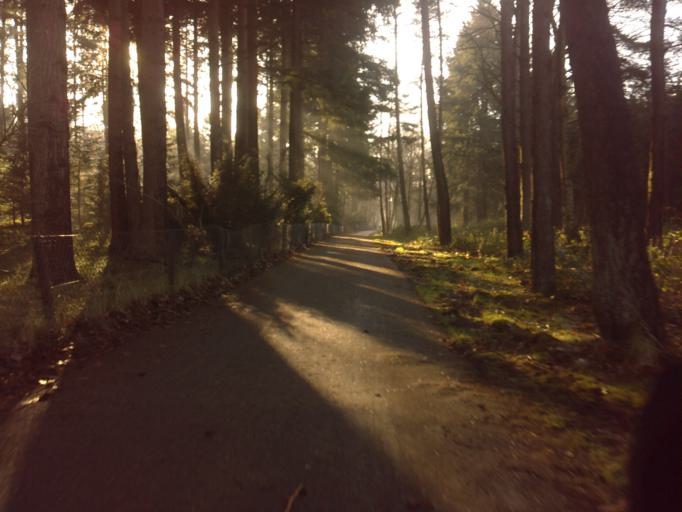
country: NL
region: Utrecht
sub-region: Gemeente Soest
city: Soest
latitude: 52.1415
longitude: 5.2765
